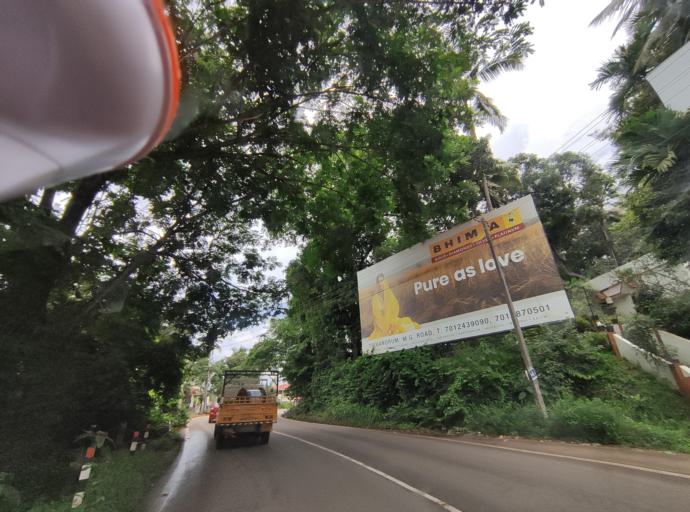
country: IN
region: Kerala
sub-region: Thiruvananthapuram
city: Nedumangad
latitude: 8.5864
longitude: 76.9499
